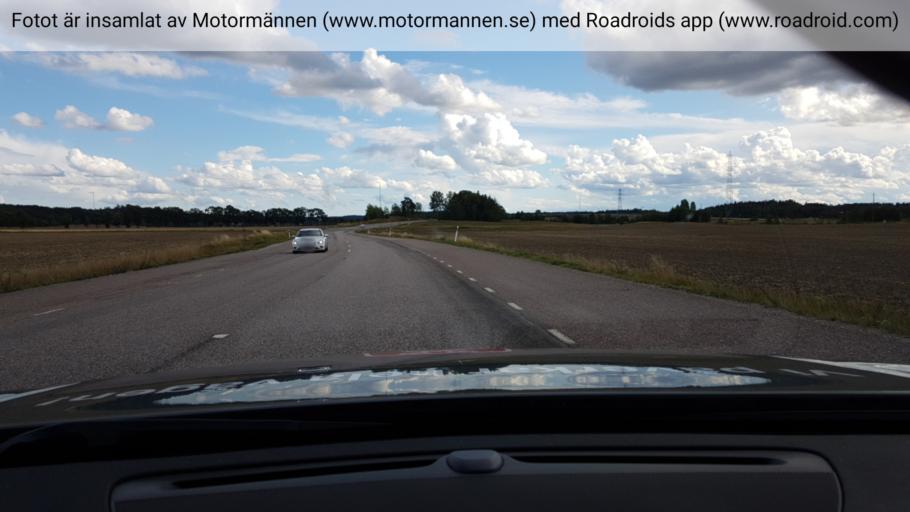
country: SE
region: Soedermanland
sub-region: Strangnas Kommun
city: Akers Styckebruk
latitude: 59.2868
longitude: 17.1091
